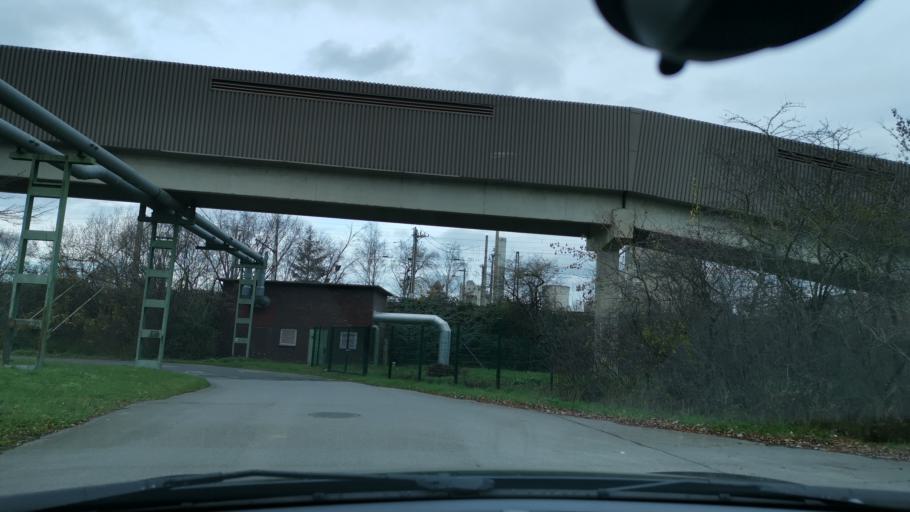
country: DE
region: North Rhine-Westphalia
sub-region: Regierungsbezirk Dusseldorf
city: Grevenbroich
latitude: 51.0503
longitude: 6.5721
